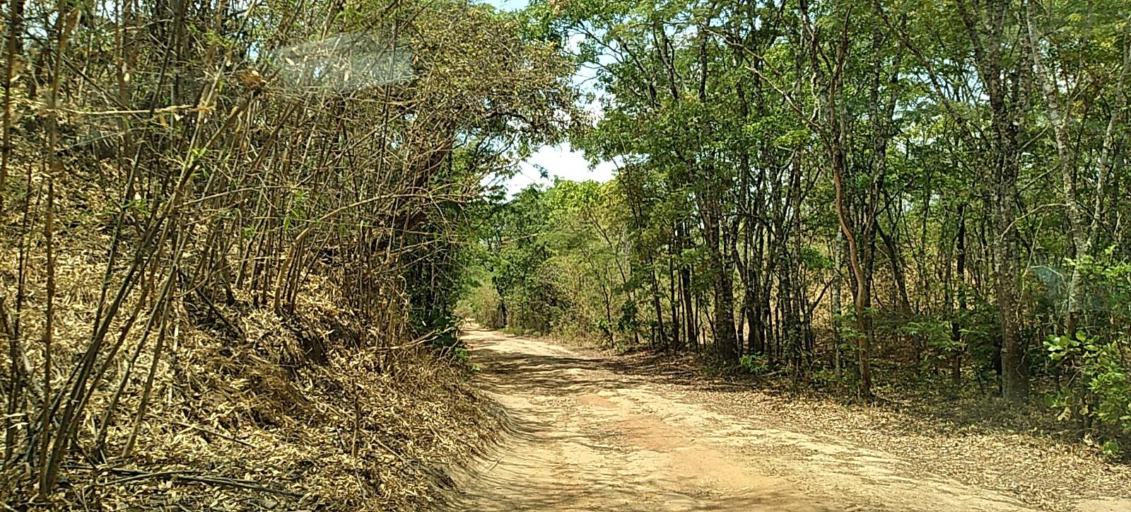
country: ZM
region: Copperbelt
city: Chililabombwe
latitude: -12.4894
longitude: 27.6383
